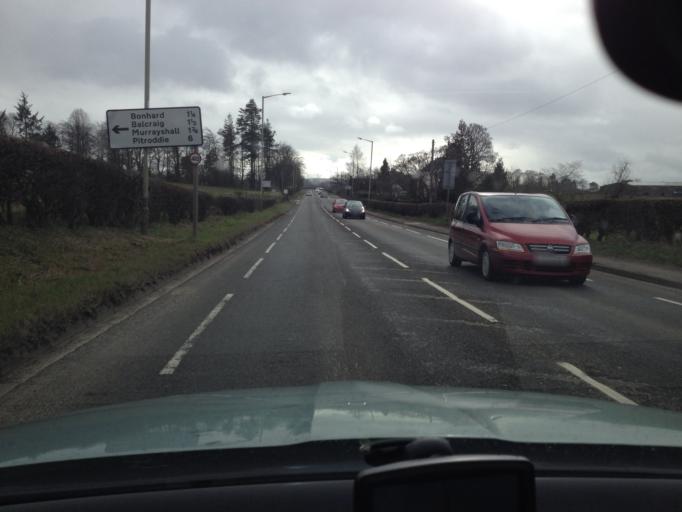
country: GB
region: Scotland
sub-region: Perth and Kinross
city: Scone
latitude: 56.4125
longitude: -3.4075
